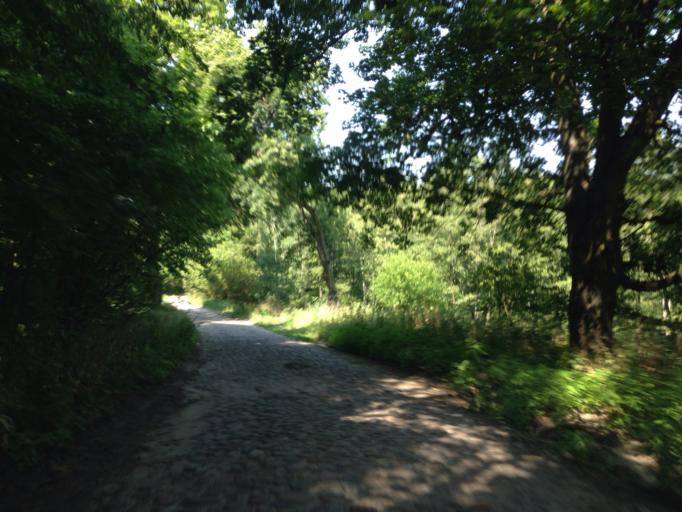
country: PL
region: Kujawsko-Pomorskie
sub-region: Powiat brodnicki
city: Gorzno
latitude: 53.2240
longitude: 19.6538
